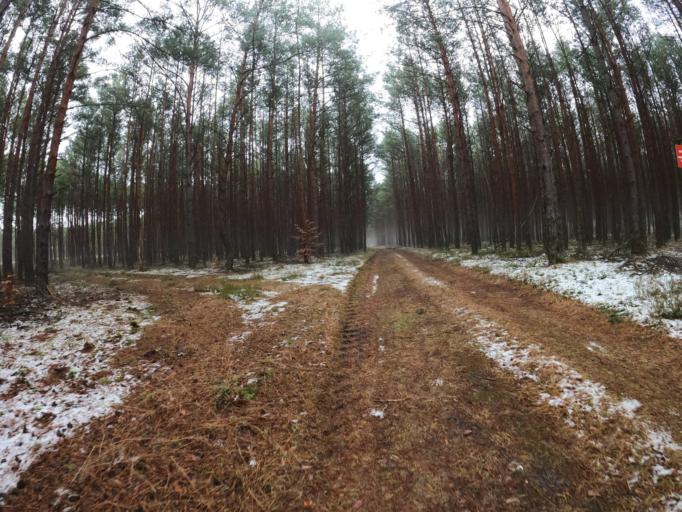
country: PL
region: Lubusz
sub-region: Powiat krosnienski
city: Maszewo
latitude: 52.2079
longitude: 14.9508
